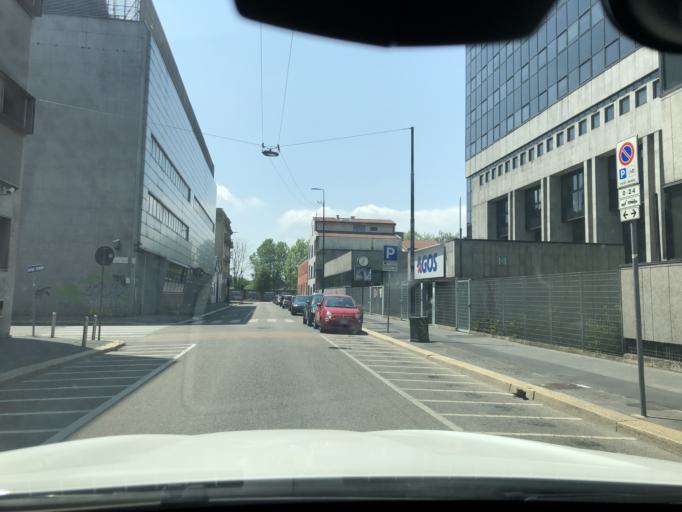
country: IT
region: Lombardy
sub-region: Citta metropolitana di Milano
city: Milano
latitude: 45.4948
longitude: 9.1809
